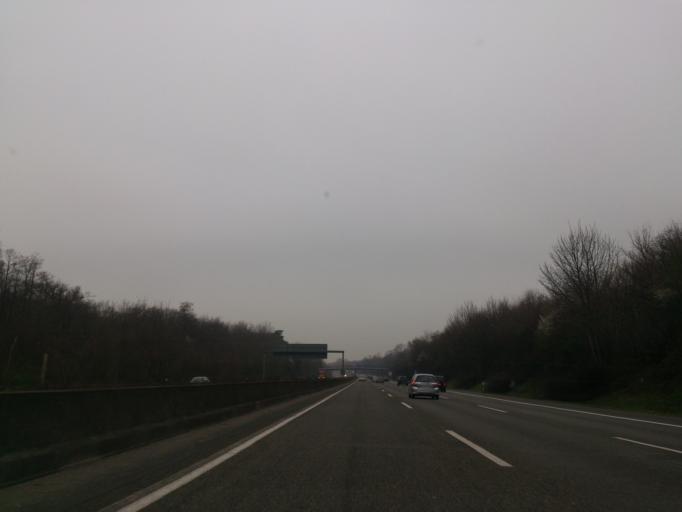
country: DE
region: North Rhine-Westphalia
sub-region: Regierungsbezirk Dusseldorf
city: Hilden
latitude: 51.1982
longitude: 6.9631
